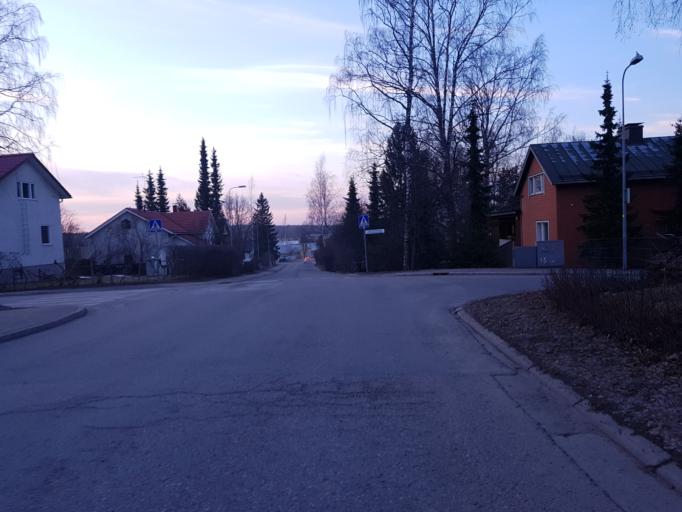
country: FI
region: Uusimaa
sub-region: Helsinki
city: Helsinki
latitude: 60.2610
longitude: 24.9525
